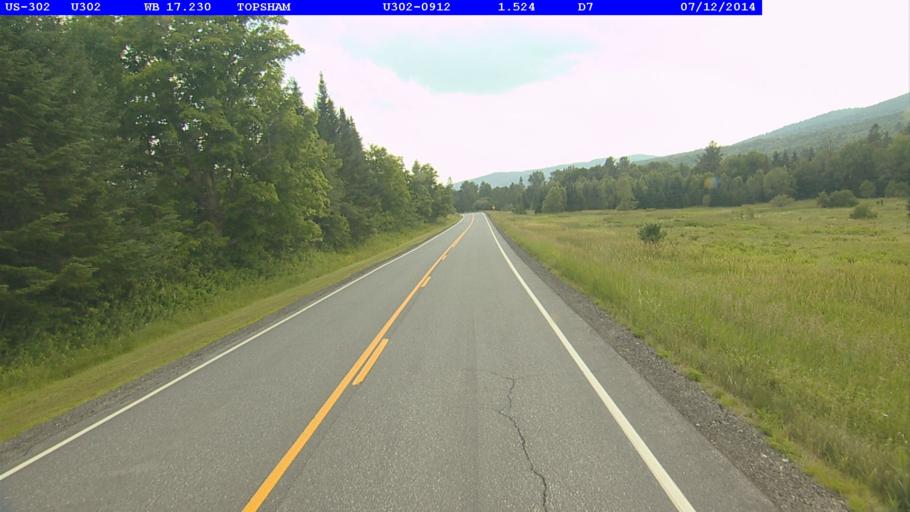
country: US
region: Vermont
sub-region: Washington County
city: Barre
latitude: 44.1586
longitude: -72.3094
